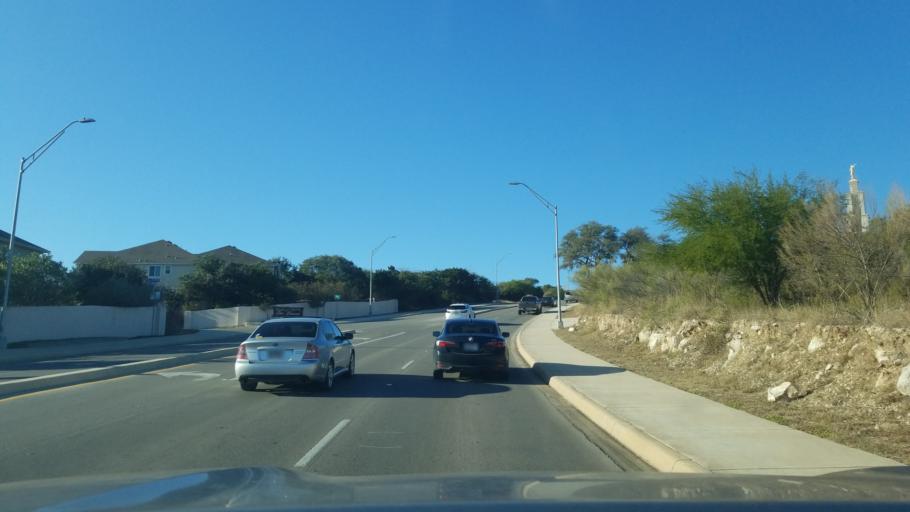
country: US
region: Texas
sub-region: Bexar County
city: Hollywood Park
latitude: 29.6395
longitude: -98.4883
